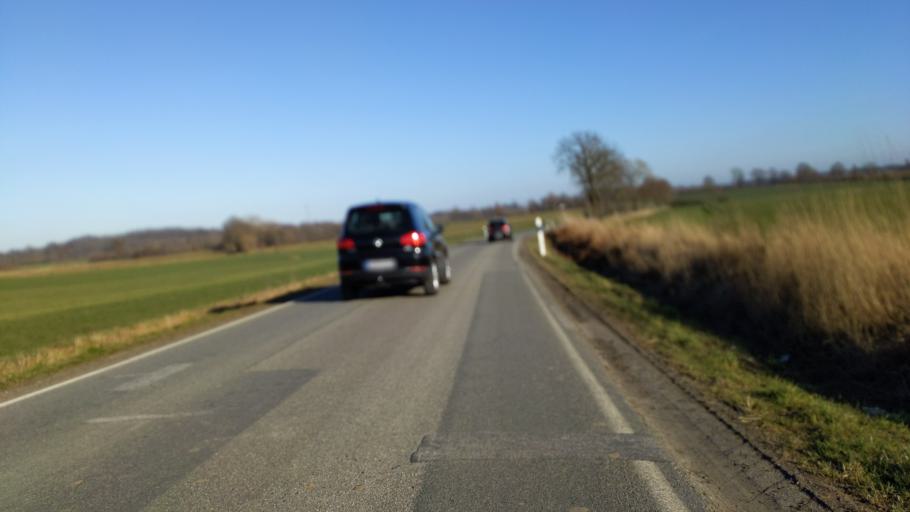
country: DE
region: Schleswig-Holstein
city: Susel
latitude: 54.0144
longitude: 10.6607
